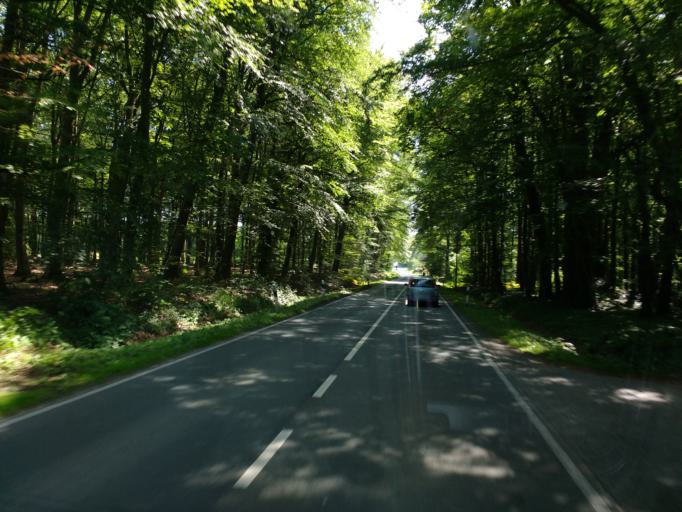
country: DE
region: Lower Saxony
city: Belm
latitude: 52.3224
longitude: 8.1120
